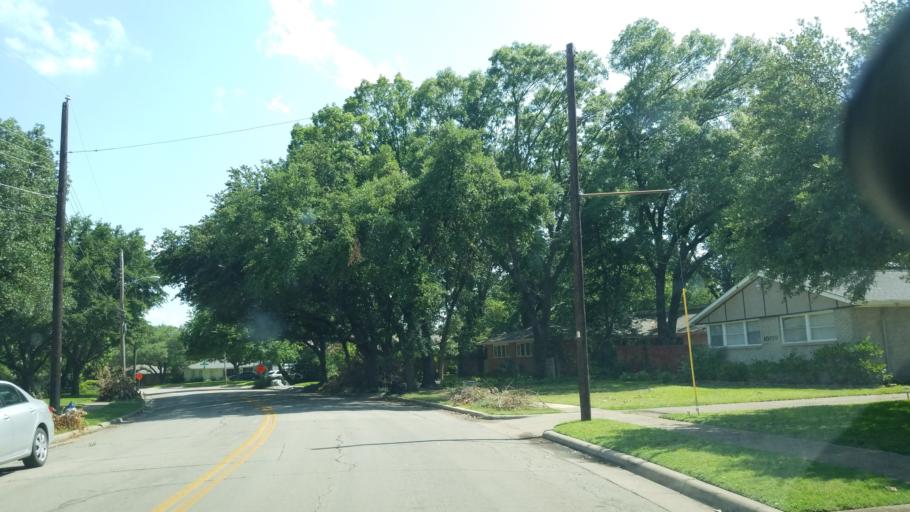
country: US
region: Texas
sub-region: Dallas County
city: Farmers Branch
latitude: 32.8840
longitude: -96.8624
